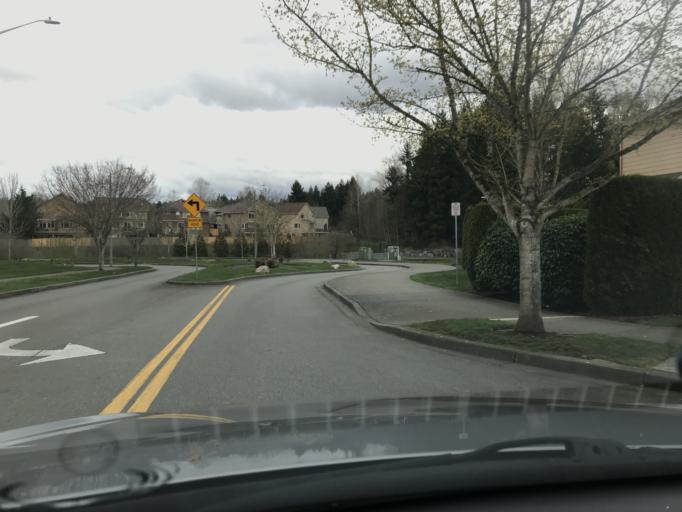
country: US
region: Washington
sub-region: King County
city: Sammamish
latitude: 47.6634
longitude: -122.0863
